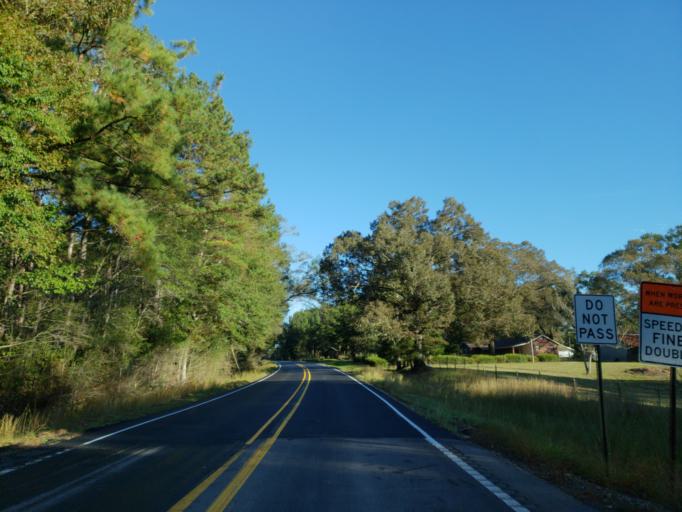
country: US
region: Mississippi
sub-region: Perry County
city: Richton
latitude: 31.3622
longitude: -88.8031
